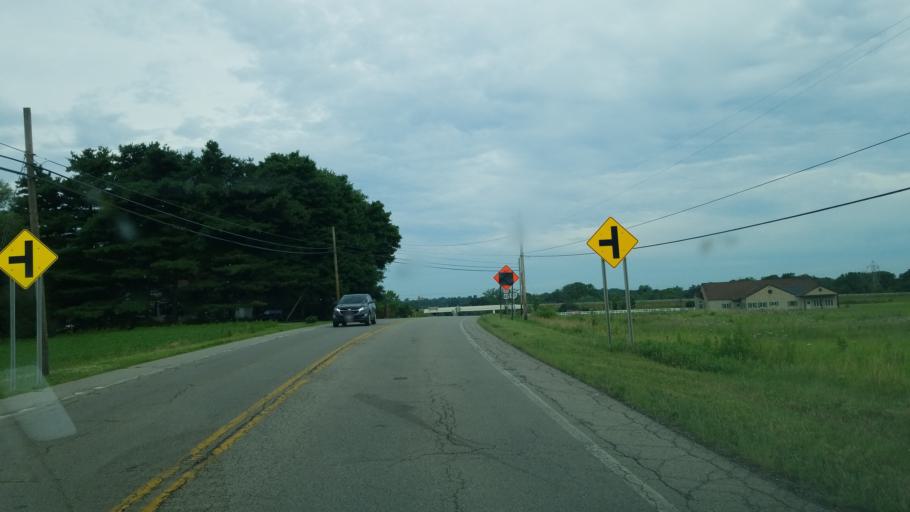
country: US
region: Ohio
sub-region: Ashland County
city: Ashland
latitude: 40.8446
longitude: -82.2950
